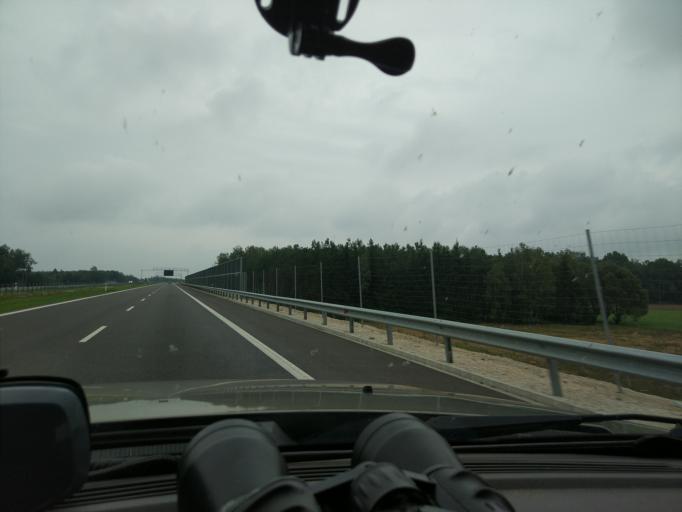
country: PL
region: Podlasie
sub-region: Powiat zambrowski
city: Szumowo
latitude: 52.9365
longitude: 22.1431
